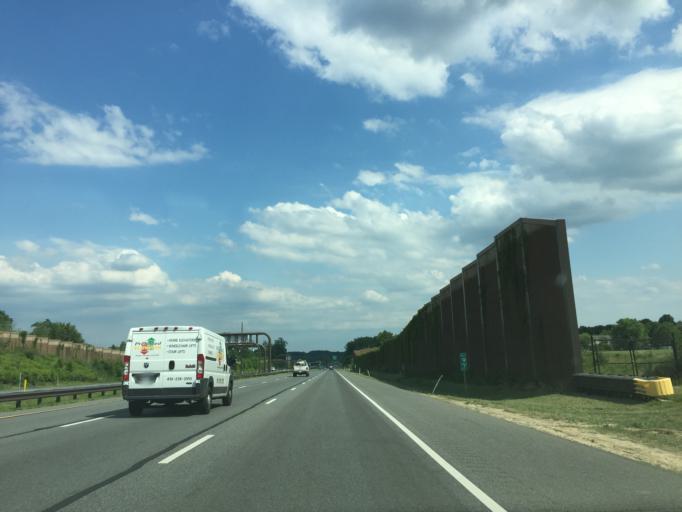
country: US
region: Maryland
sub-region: Montgomery County
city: Leisure World
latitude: 39.1067
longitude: -77.0534
